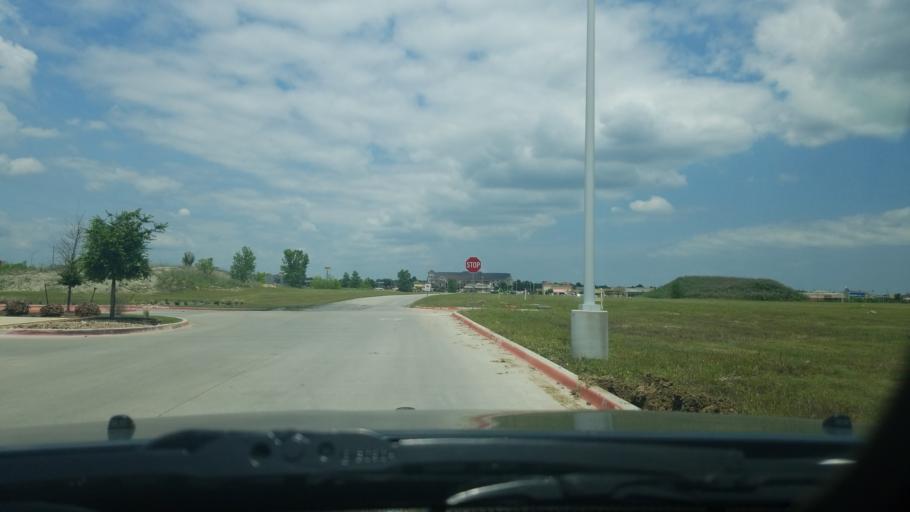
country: US
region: Texas
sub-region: Denton County
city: Denton
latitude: 33.2254
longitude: -97.1709
